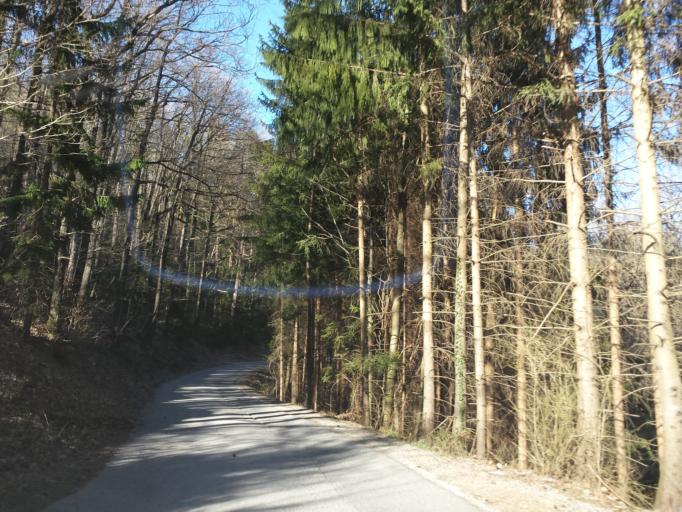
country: AT
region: Styria
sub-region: Politischer Bezirk Graz-Umgebung
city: Sankt Radegund bei Graz
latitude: 47.1568
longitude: 15.4623
